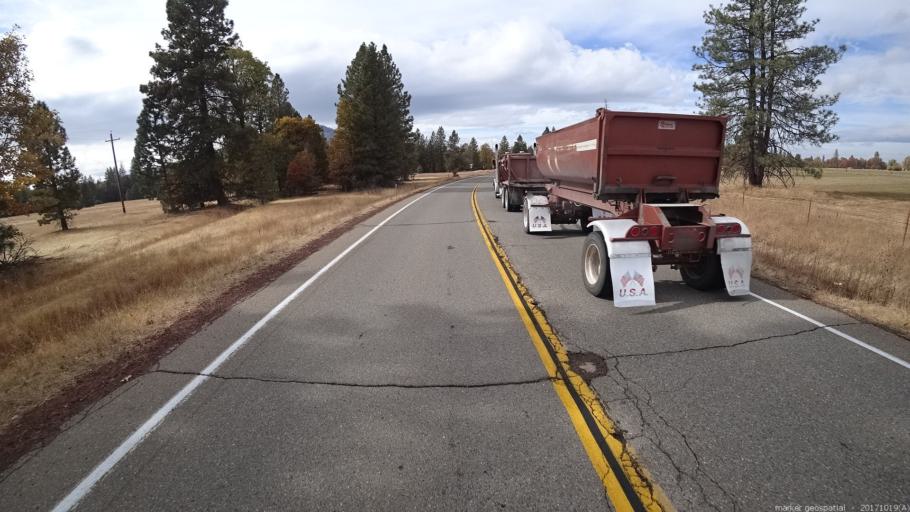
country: US
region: California
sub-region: Shasta County
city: Burney
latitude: 41.0800
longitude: -121.5117
